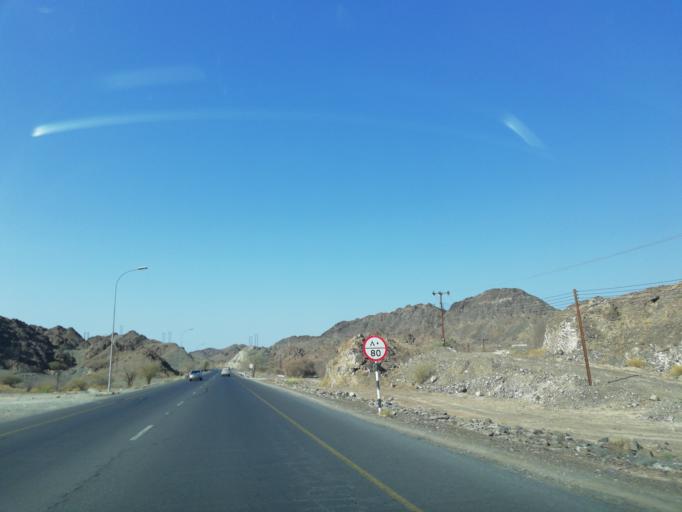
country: OM
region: Ash Sharqiyah
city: Ibra'
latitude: 22.8238
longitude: 58.1685
